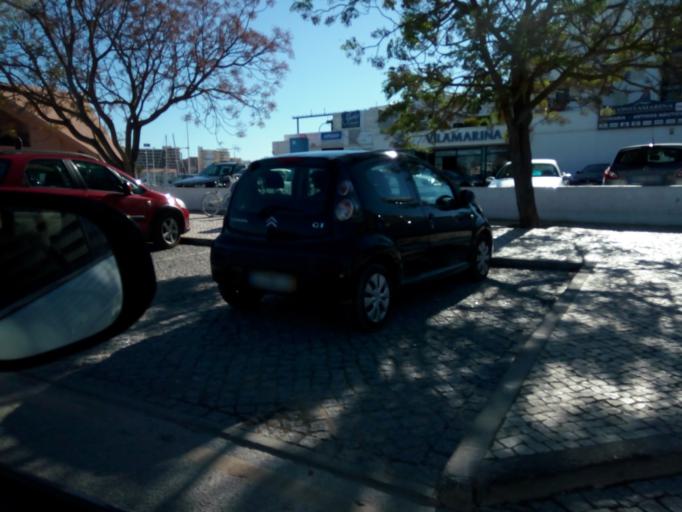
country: PT
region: Faro
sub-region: Loule
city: Vilamoura
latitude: 37.0792
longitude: -8.1223
